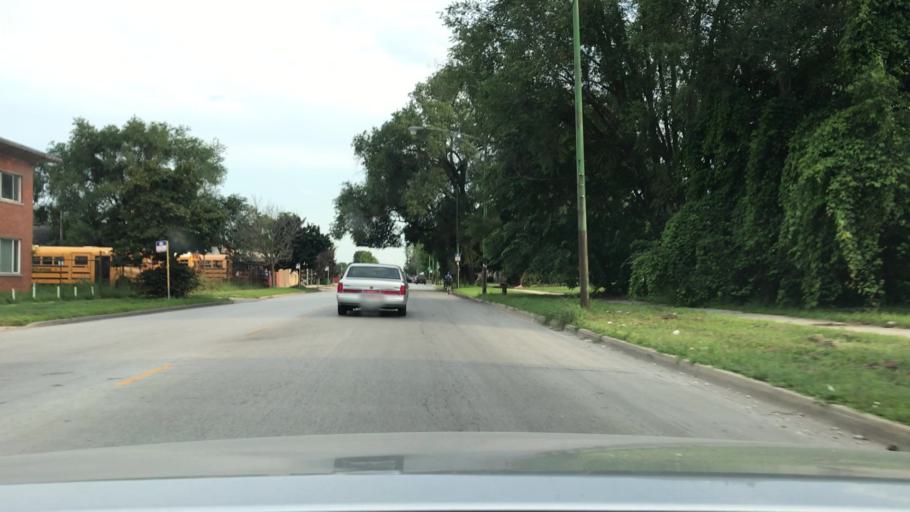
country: US
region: Indiana
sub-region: Lake County
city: Whiting
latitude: 41.7131
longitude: -87.5598
